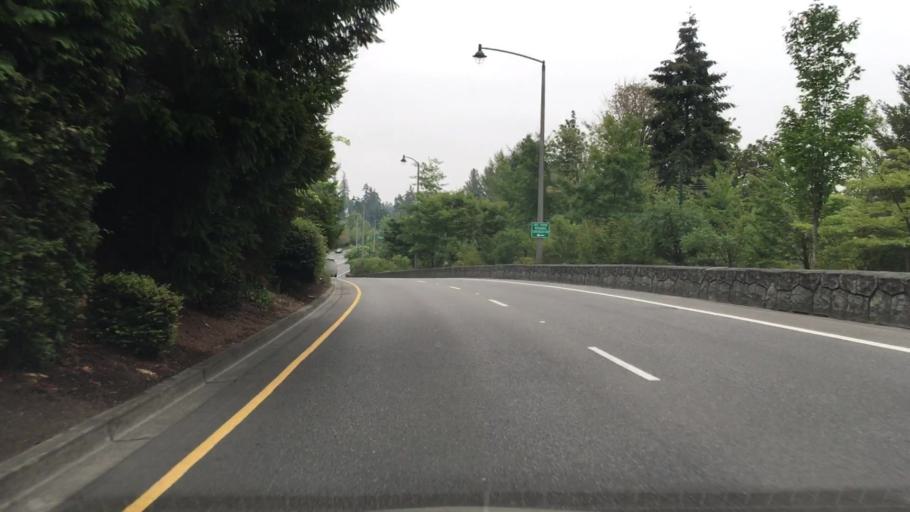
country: US
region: Washington
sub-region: King County
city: Newcastle
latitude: 47.5338
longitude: -122.1640
